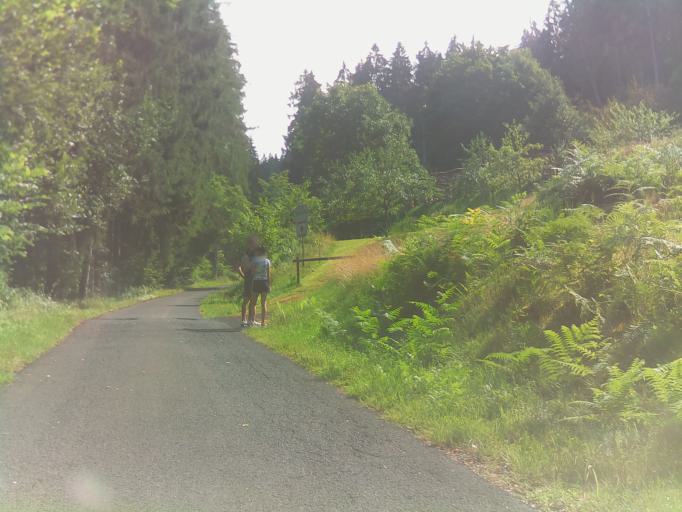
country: DE
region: Hesse
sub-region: Regierungsbezirk Darmstadt
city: Bad Orb
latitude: 50.2079
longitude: 9.3530
